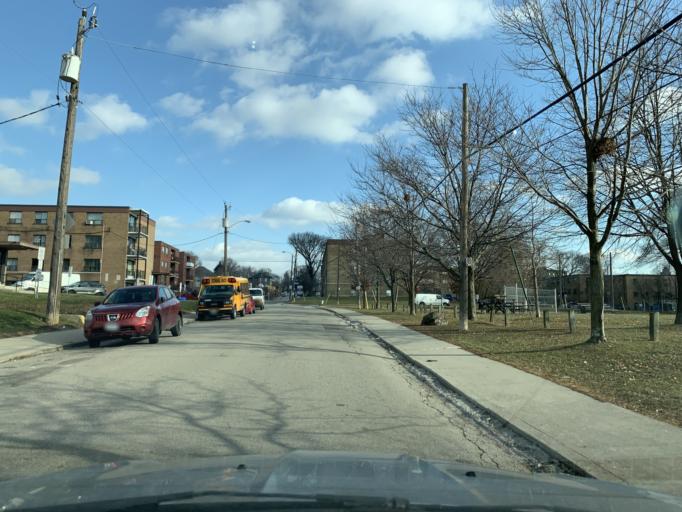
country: CA
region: Ontario
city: Toronto
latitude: 43.6925
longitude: -79.4812
